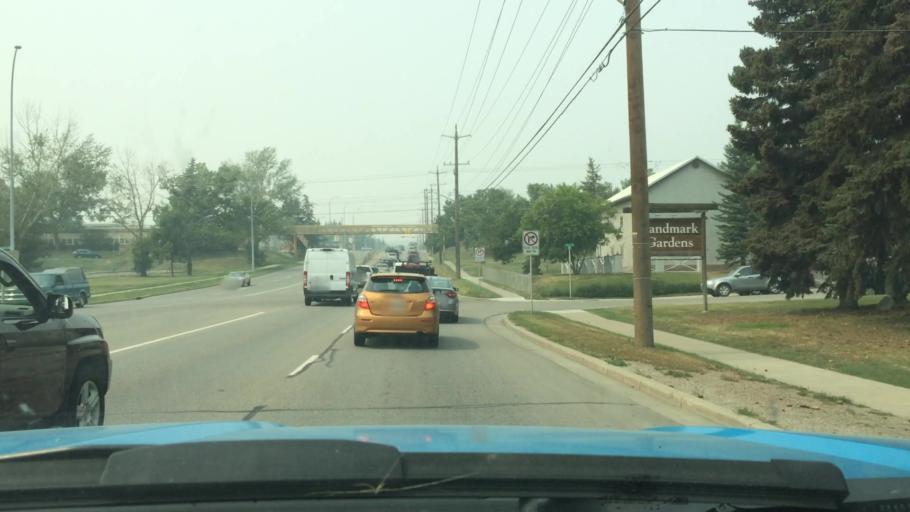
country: CA
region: Alberta
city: Calgary
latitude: 51.0962
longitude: -114.0576
